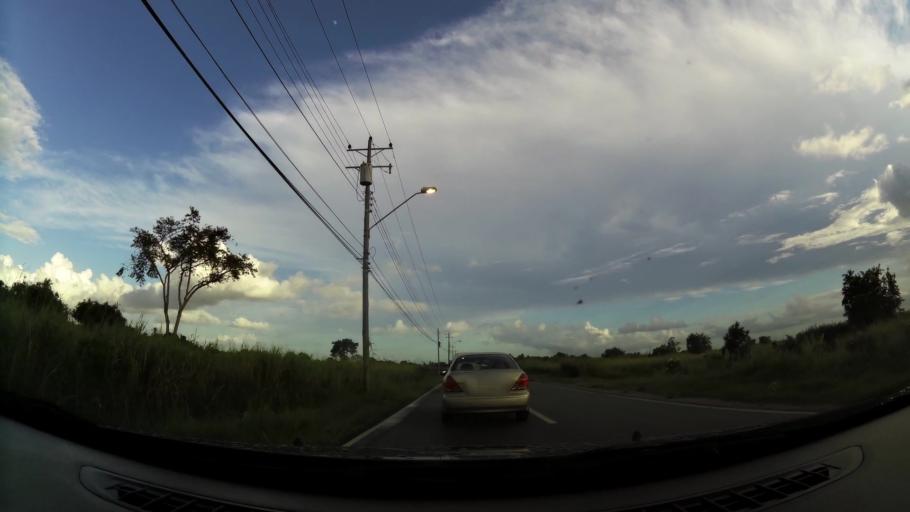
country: TT
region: Tunapuna/Piarco
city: Tunapuna
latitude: 10.5982
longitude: -61.3706
